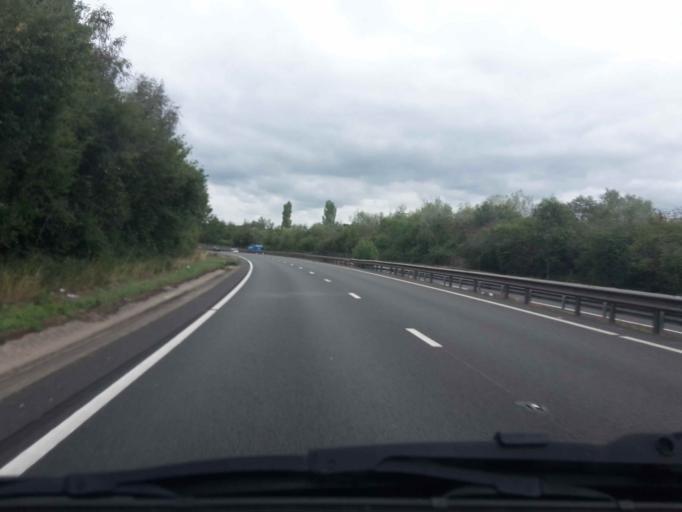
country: GB
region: England
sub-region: Surrey
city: Seale
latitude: 51.2517
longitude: -0.7302
